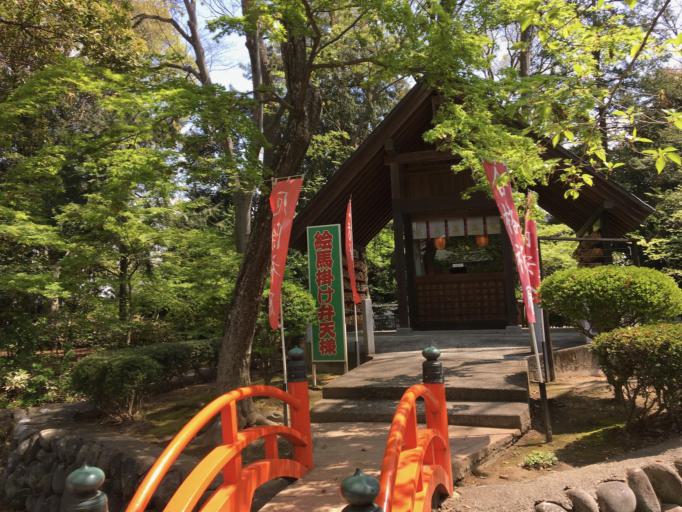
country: JP
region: Gunma
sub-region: Sawa-gun
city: Tamamura
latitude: 36.3050
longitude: 139.1090
